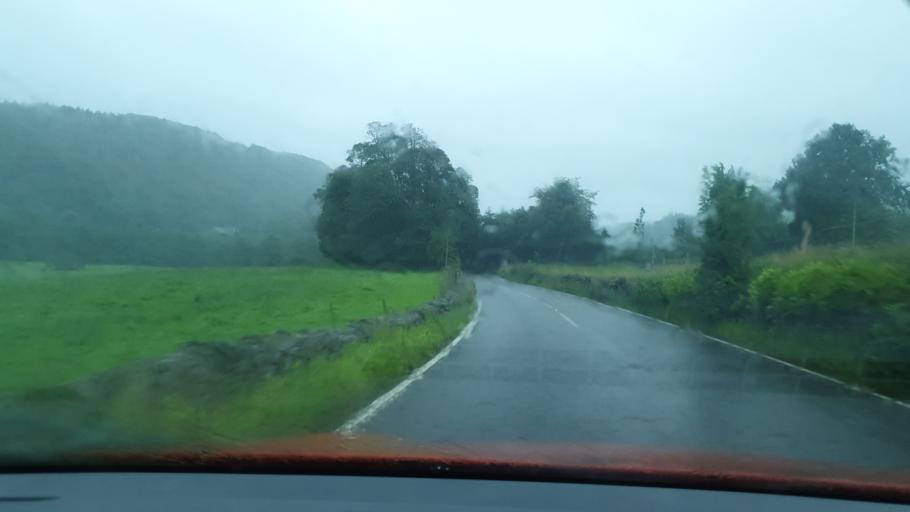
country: GB
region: England
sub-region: Cumbria
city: Ulverston
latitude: 54.2483
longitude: -3.0678
